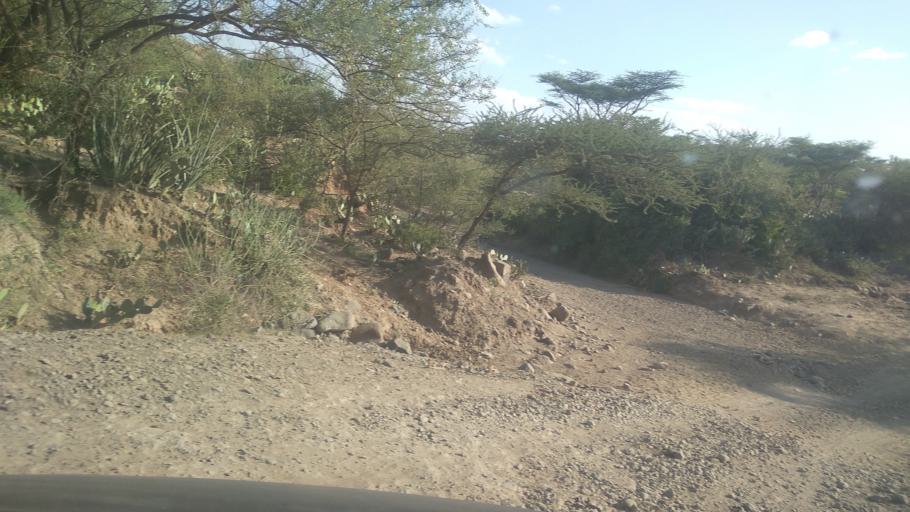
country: ET
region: Oromiya
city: Hirna
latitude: 9.4350
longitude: 40.9804
